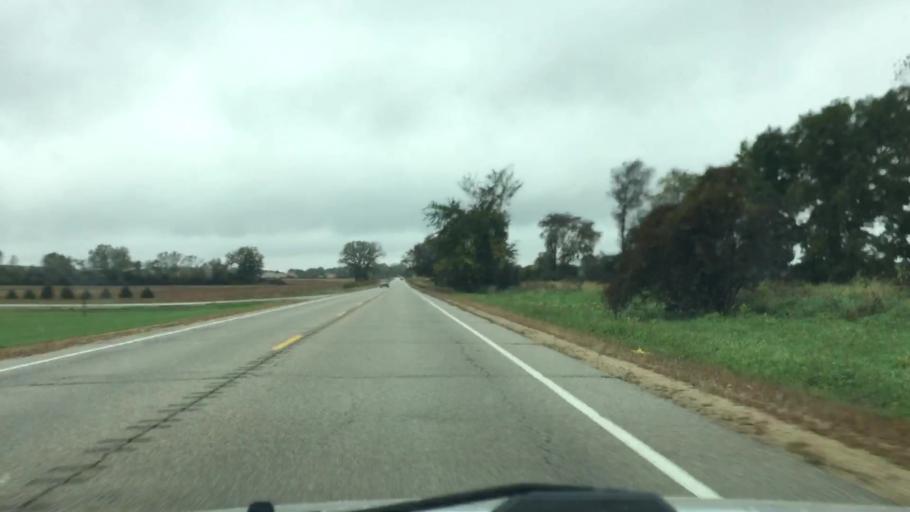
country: US
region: Wisconsin
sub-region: Walworth County
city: Whitewater
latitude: 42.7991
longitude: -88.8016
